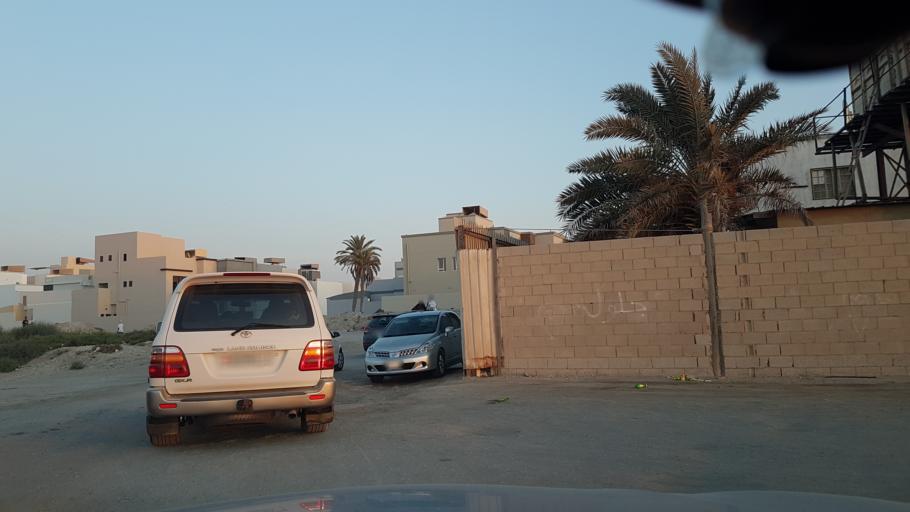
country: BH
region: Manama
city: Jidd Hafs
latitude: 26.2359
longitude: 50.5055
